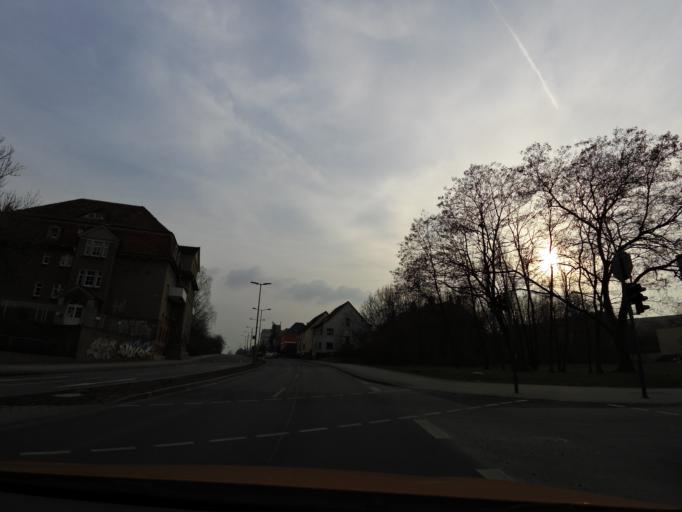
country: DE
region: Brandenburg
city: Frankfurt (Oder)
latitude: 52.3335
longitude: 14.5346
